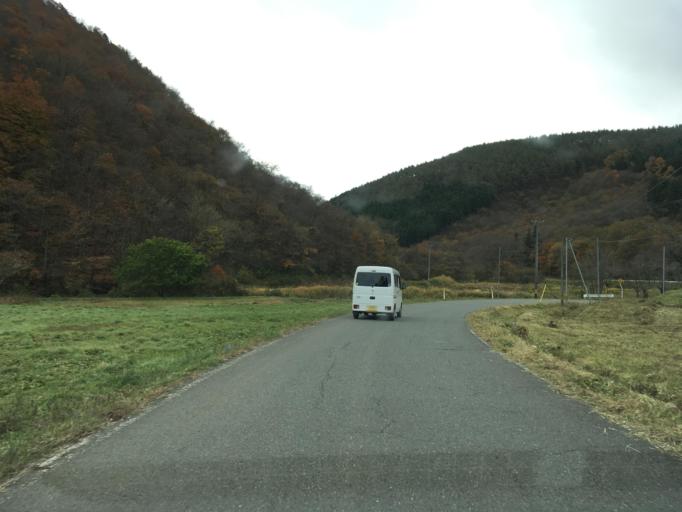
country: JP
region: Iwate
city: Mizusawa
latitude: 39.1063
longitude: 141.3293
